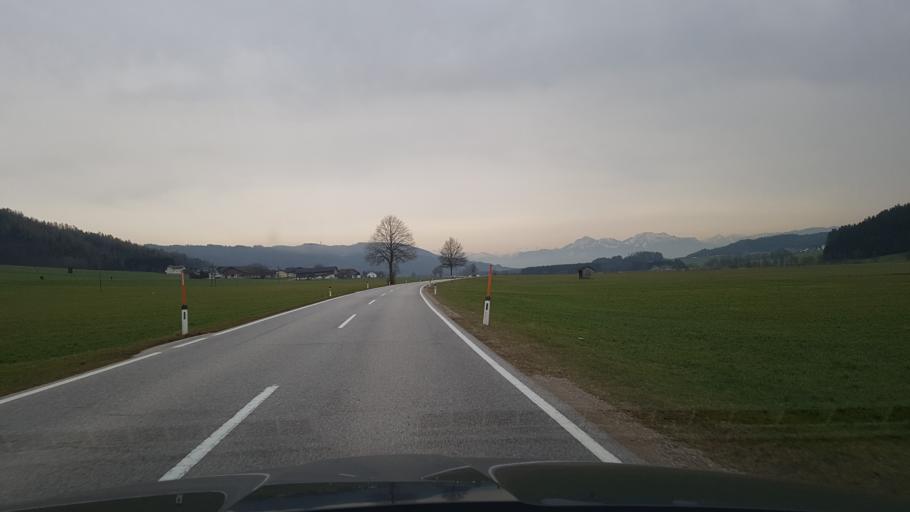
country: AT
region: Salzburg
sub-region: Politischer Bezirk Salzburg-Umgebung
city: Nussdorf am Haunsberg
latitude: 47.9814
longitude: 13.0118
